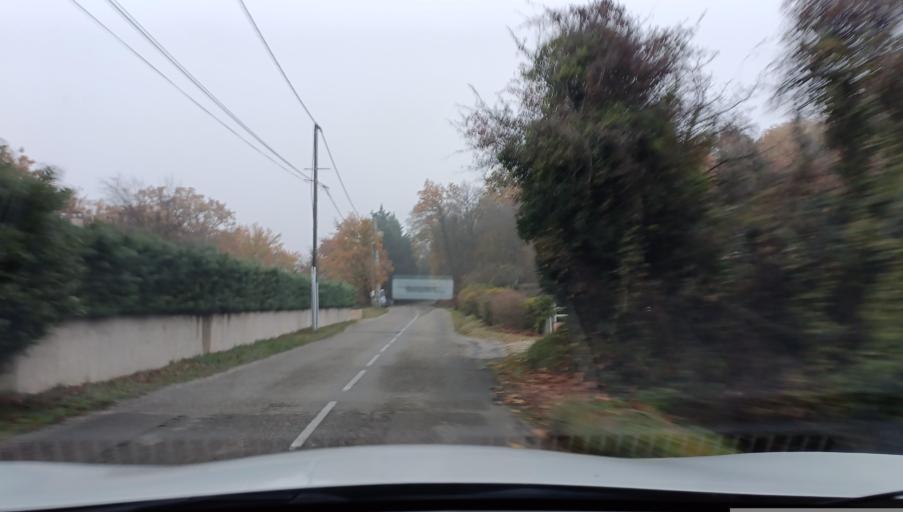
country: FR
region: Rhone-Alpes
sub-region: Departement de l'Isere
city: Serpaize
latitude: 45.5486
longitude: 4.9252
